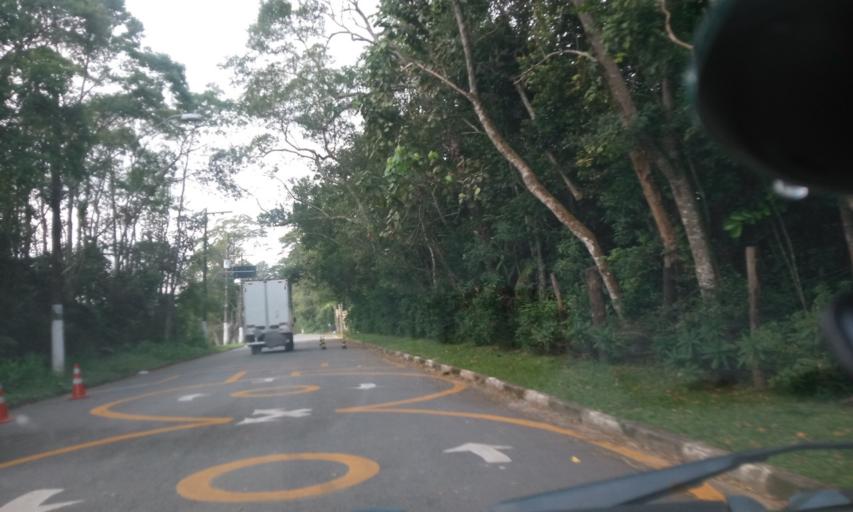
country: BR
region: Sao Paulo
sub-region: Sao Bernardo Do Campo
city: Sao Bernardo do Campo
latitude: -23.7863
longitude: -46.5403
